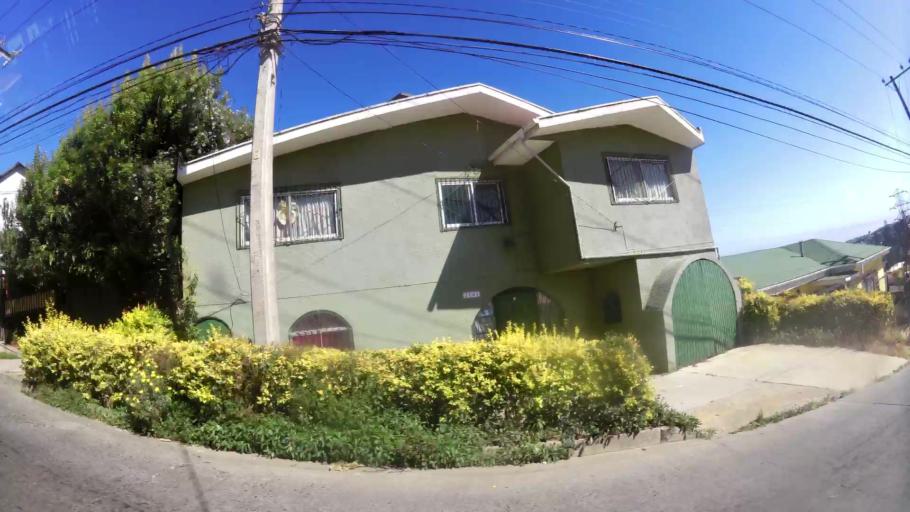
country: CL
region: Valparaiso
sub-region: Provincia de Valparaiso
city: Valparaiso
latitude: -33.0697
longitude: -71.5830
